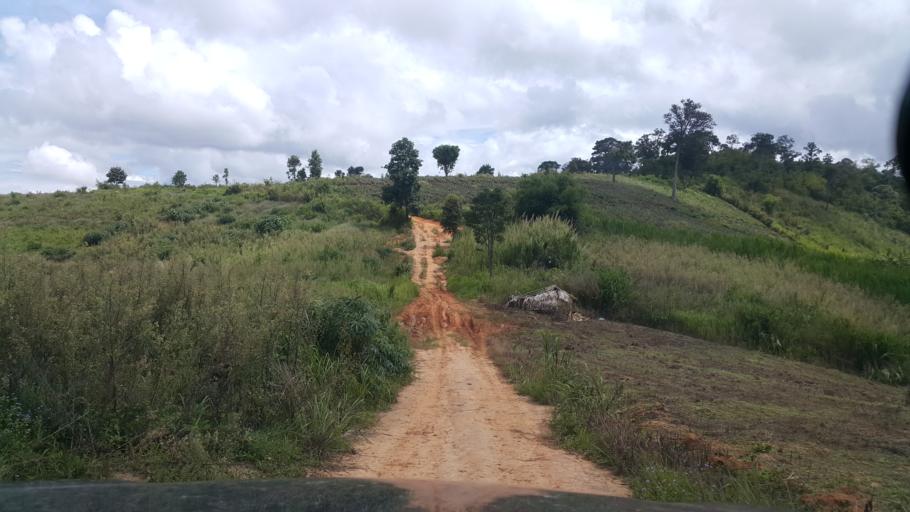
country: TH
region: Loei
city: Na Haeo
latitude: 17.5919
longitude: 100.8894
